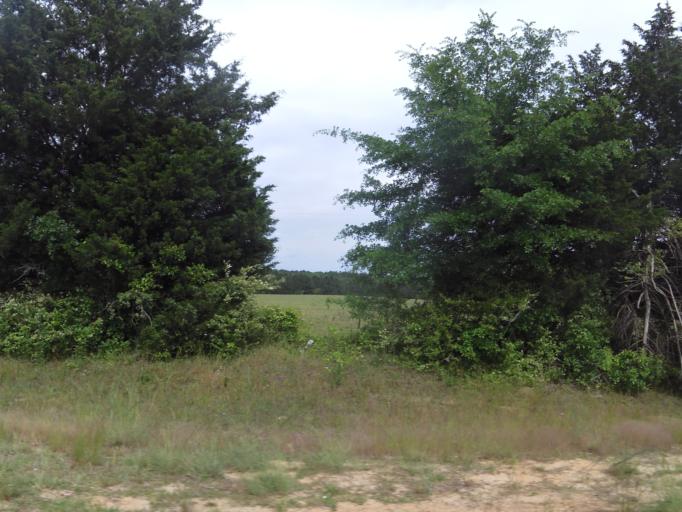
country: US
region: Georgia
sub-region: McDuffie County
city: Thomson
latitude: 33.3636
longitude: -82.4655
